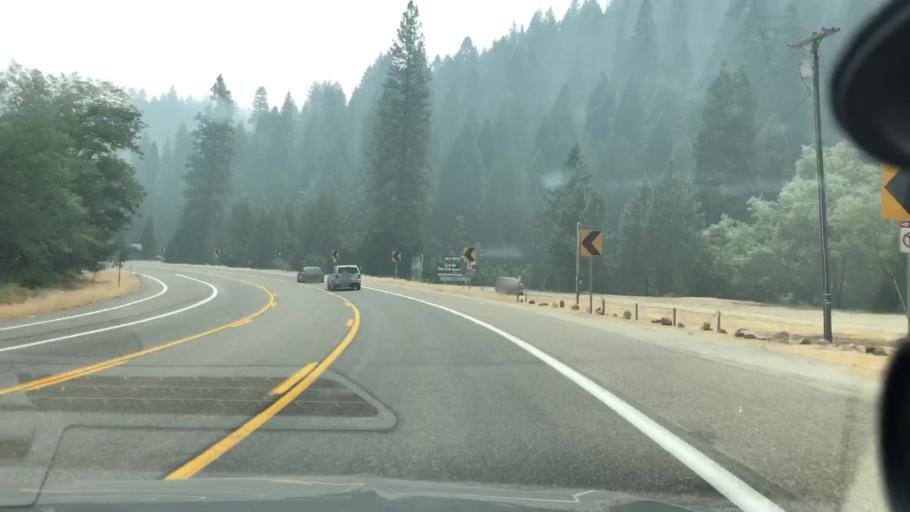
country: US
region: California
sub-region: El Dorado County
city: Pollock Pines
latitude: 38.7691
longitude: -120.4472
